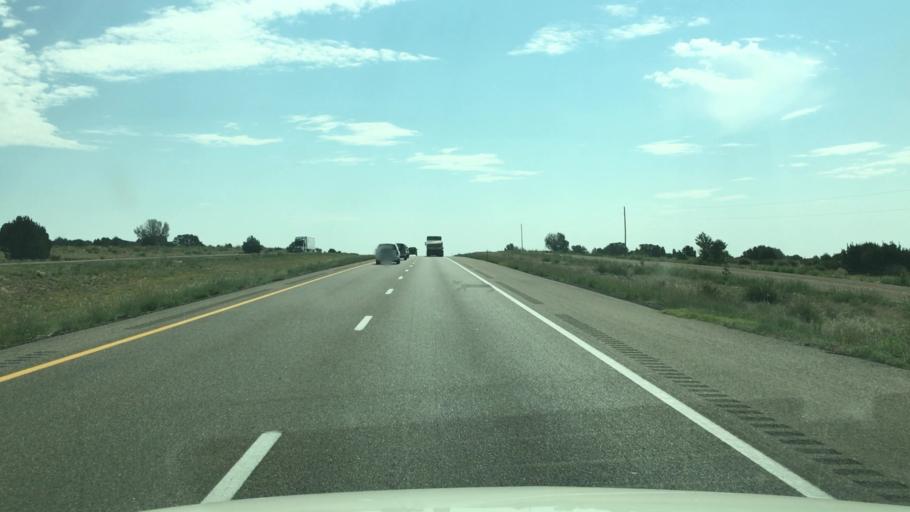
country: US
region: New Mexico
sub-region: Guadalupe County
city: Santa Rosa
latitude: 34.9713
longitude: -104.8938
